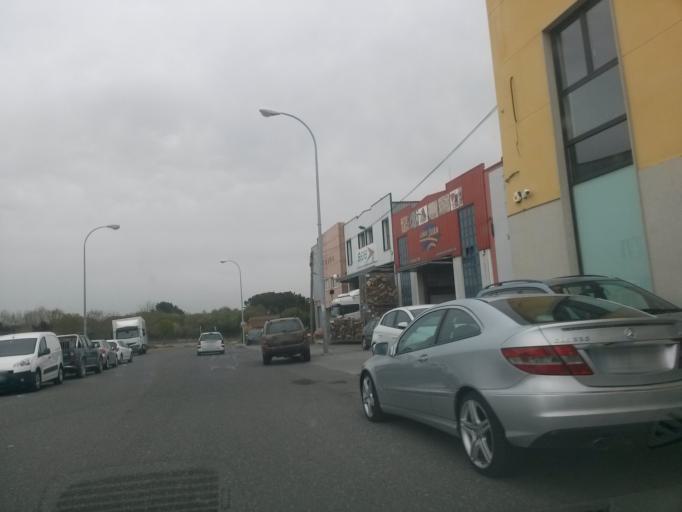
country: ES
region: Galicia
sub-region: Provincia de Lugo
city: Lugo
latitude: 43.0421
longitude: -7.5604
